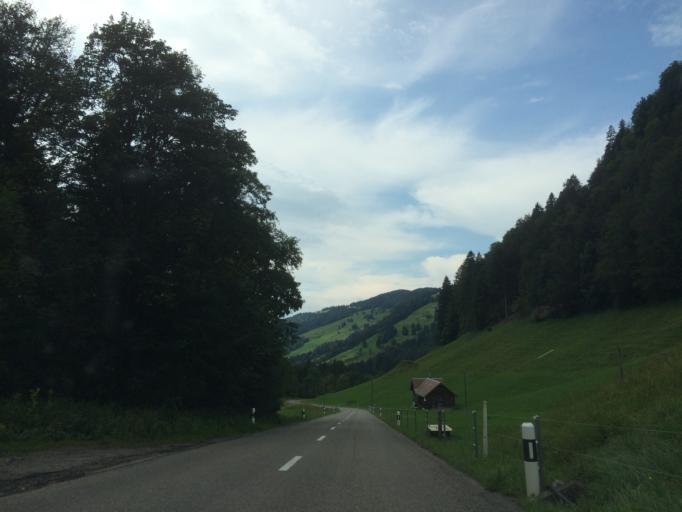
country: CH
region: Appenzell Ausserrhoden
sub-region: Bezirk Hinterland
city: Urnasch
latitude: 47.2427
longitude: 9.2679
